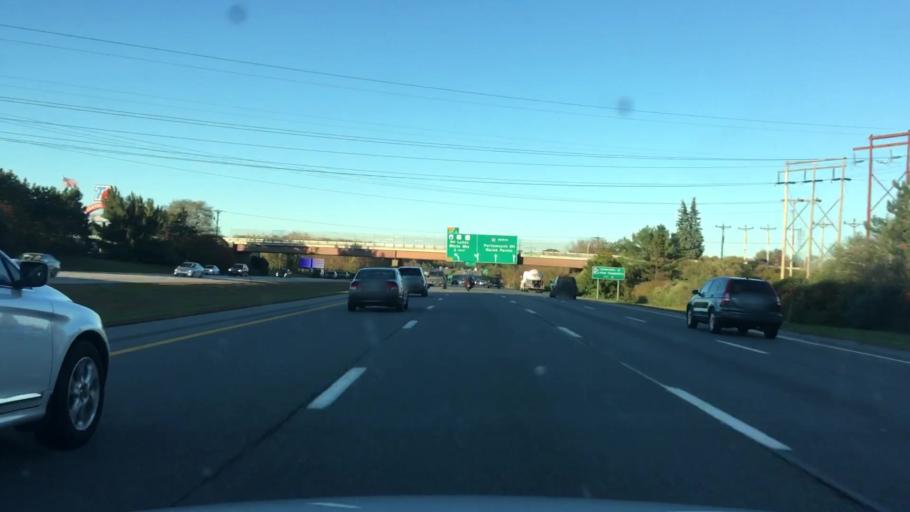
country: US
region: New Hampshire
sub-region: Rockingham County
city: Greenland
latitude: 43.0409
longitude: -70.8174
